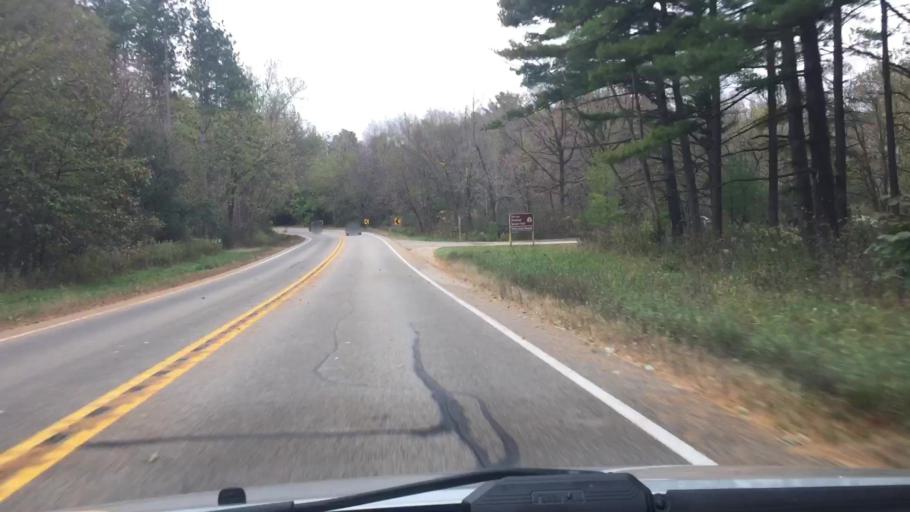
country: US
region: Wisconsin
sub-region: Waukesha County
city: Eagle
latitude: 42.9192
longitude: -88.4725
